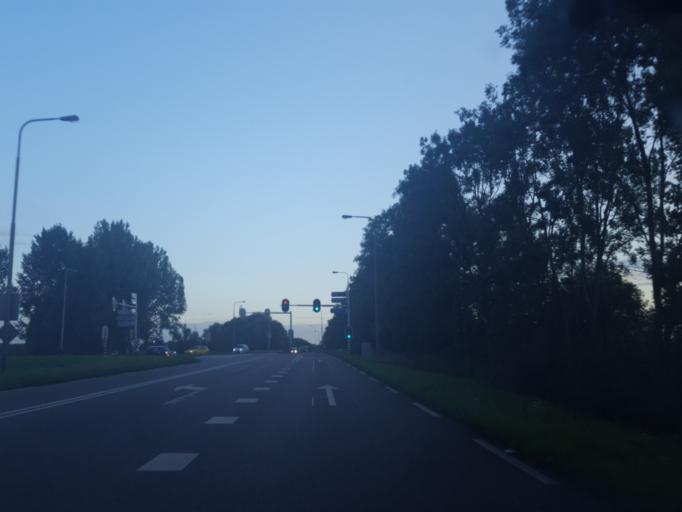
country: NL
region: Gelderland
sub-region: Gemeente Beuningen
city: Beuningen
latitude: 51.8535
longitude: 5.7487
